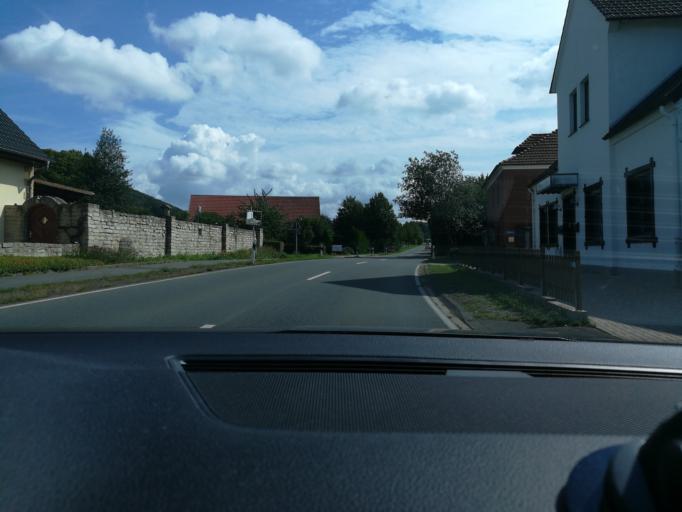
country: DE
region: North Rhine-Westphalia
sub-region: Regierungsbezirk Detmold
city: Hille
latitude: 52.2744
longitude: 8.7321
